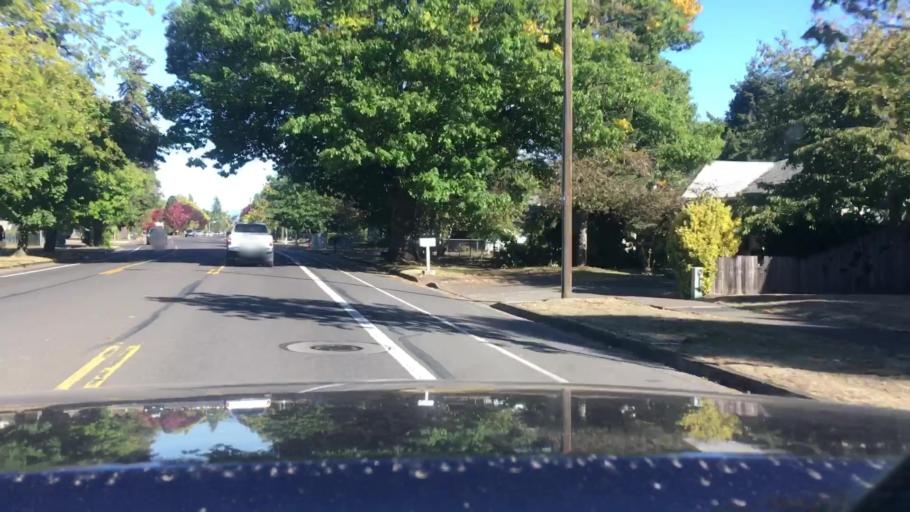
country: US
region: Oregon
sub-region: Lane County
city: Eugene
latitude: 44.0696
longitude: -123.0610
